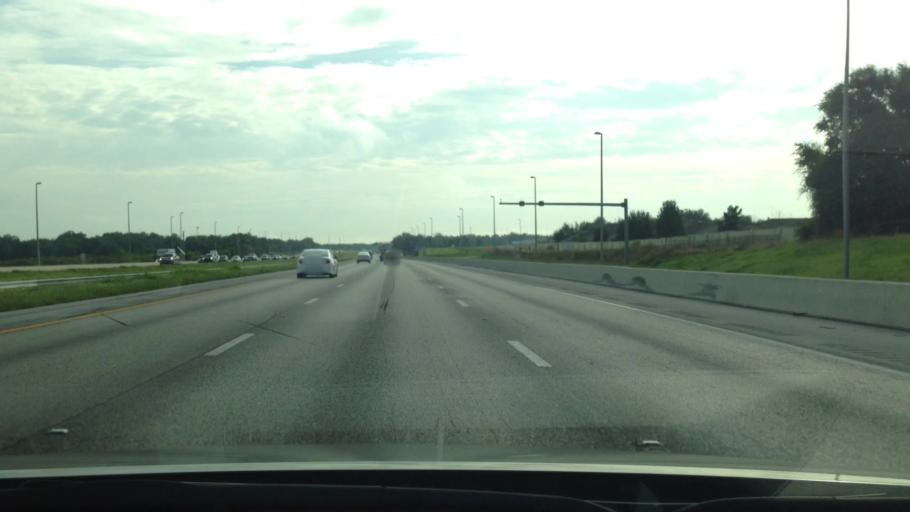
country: US
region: Florida
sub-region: Hillsborough County
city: Seffner
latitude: 28.0131
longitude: -82.2731
